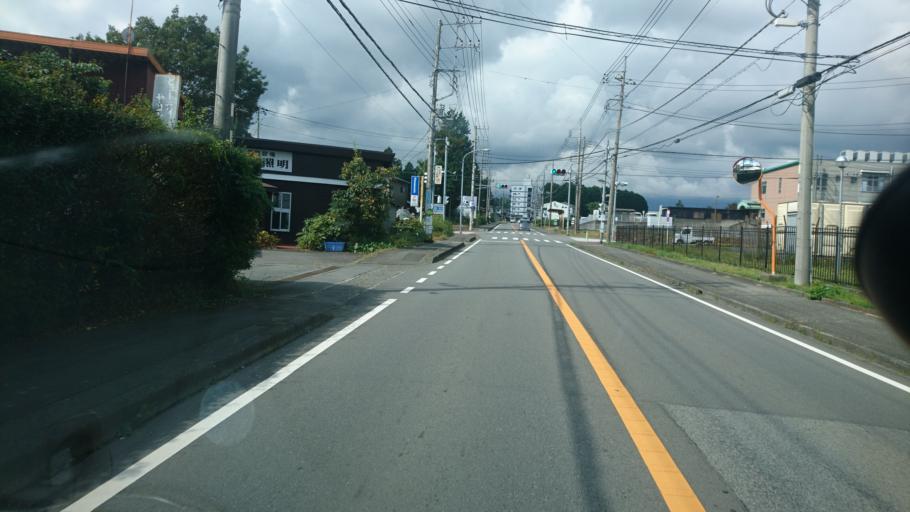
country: JP
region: Shizuoka
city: Gotemba
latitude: 35.3079
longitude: 138.9140
